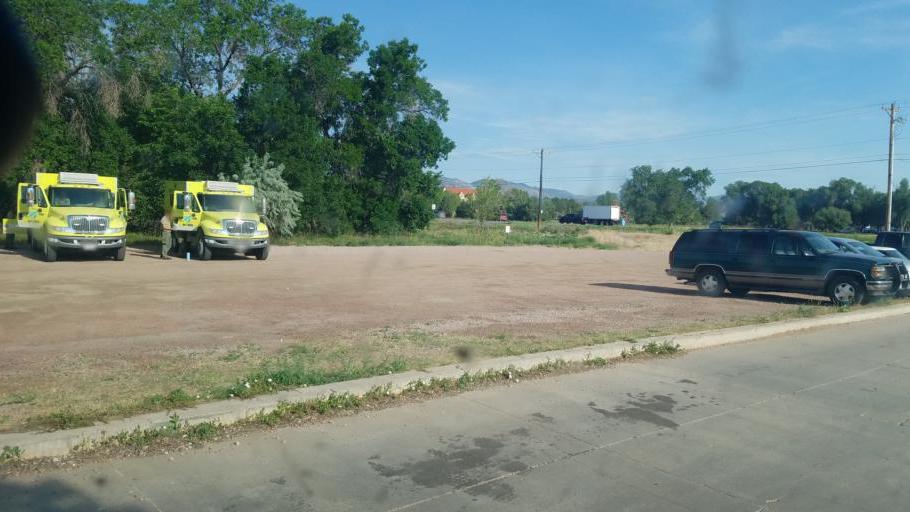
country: US
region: Colorado
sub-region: Fremont County
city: Lincoln Park
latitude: 38.4461
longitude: -105.1966
